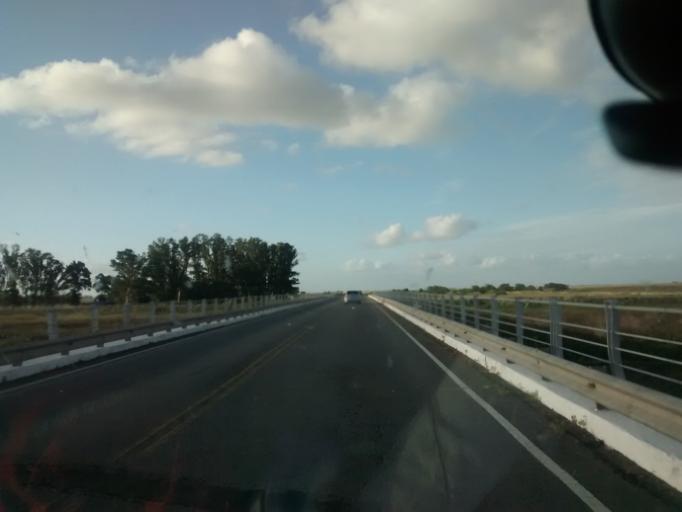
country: AR
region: Buenos Aires
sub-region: Partido de General Belgrano
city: General Belgrano
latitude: -36.1371
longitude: -58.5941
